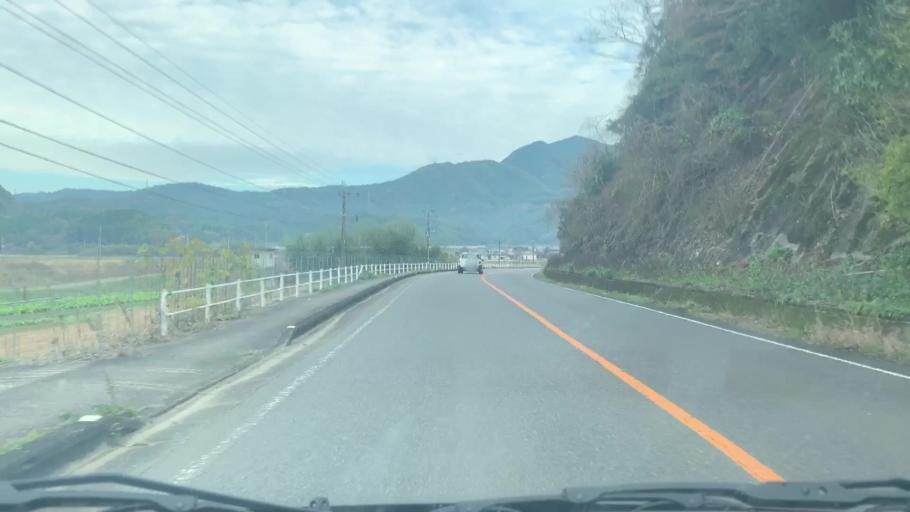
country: JP
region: Saga Prefecture
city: Takeocho-takeo
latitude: 33.2531
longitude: 129.9708
